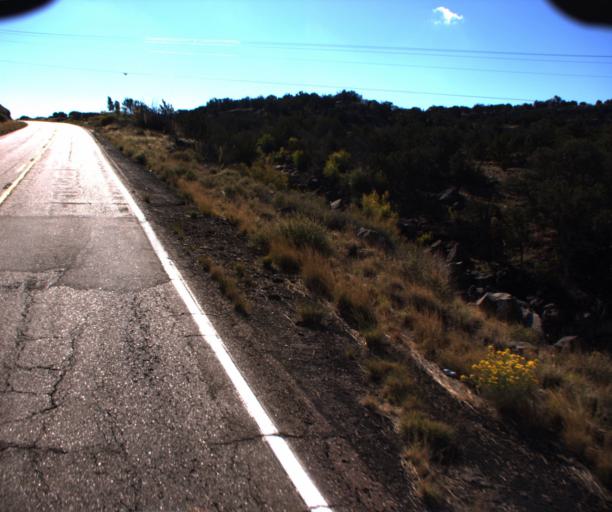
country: US
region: Arizona
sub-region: Apache County
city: Saint Johns
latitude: 34.4836
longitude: -109.5723
